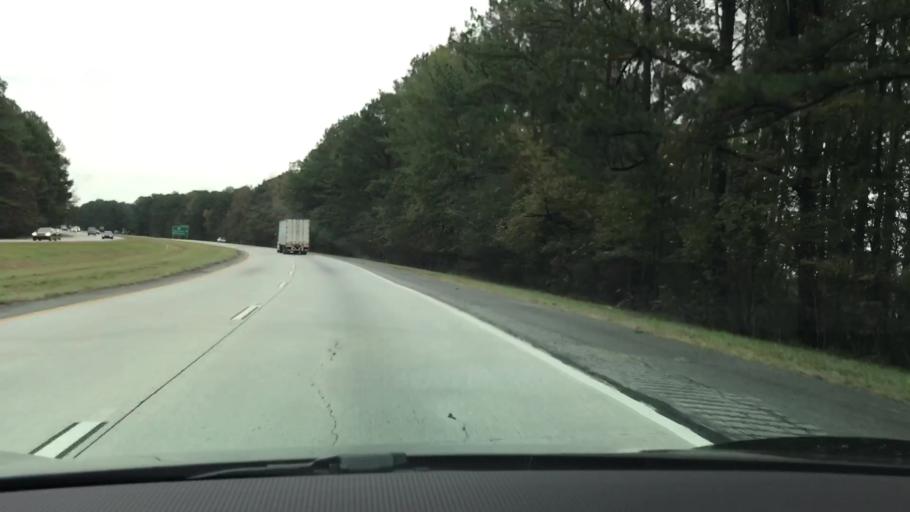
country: US
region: Georgia
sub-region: Taliaferro County
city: Crawfordville
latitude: 33.4980
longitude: -82.8150
